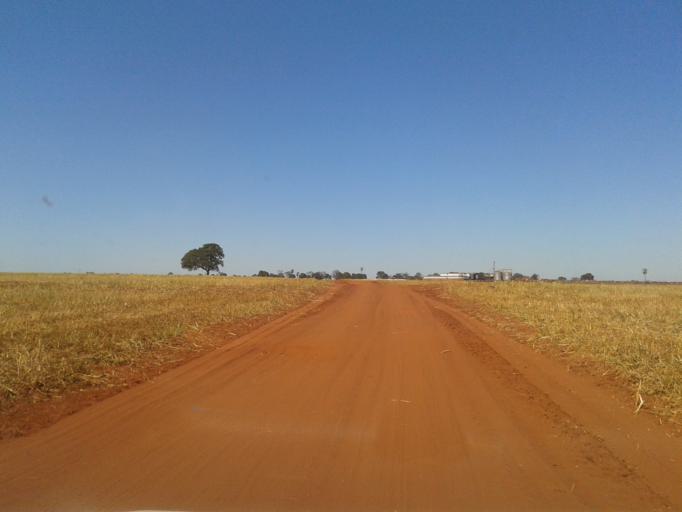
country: BR
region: Minas Gerais
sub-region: Santa Vitoria
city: Santa Vitoria
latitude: -19.2304
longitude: -50.2087
